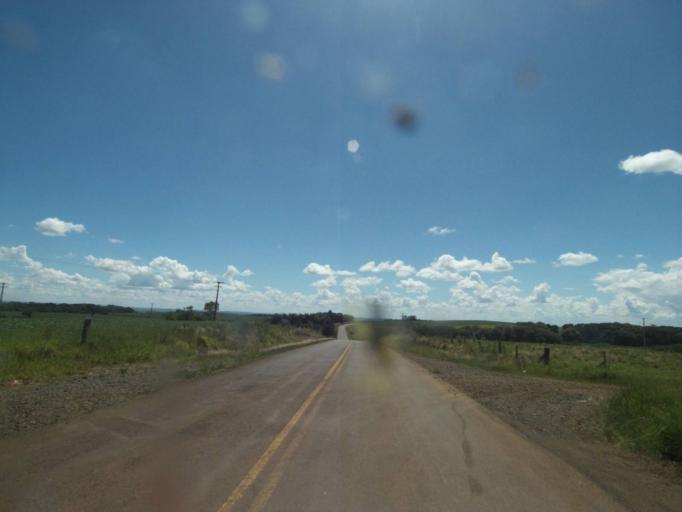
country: BR
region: Parana
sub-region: Pinhao
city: Pinhao
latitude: -25.8131
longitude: -52.0608
